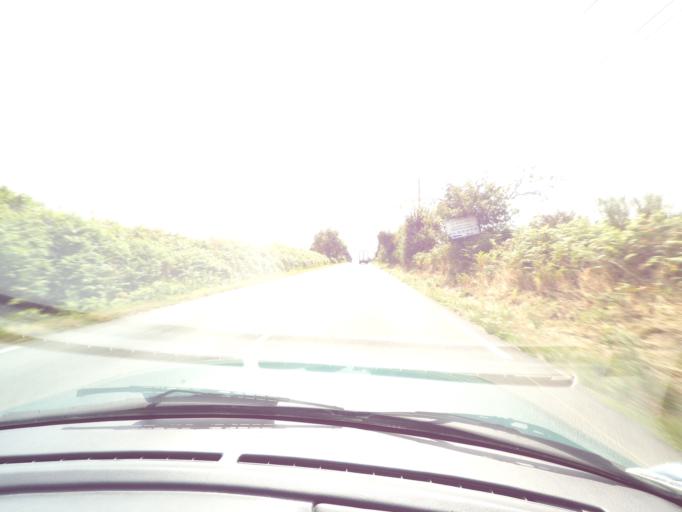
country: FR
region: Limousin
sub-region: Departement de la Haute-Vienne
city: Neuvic-Entier
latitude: 45.7391
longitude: 1.6092
